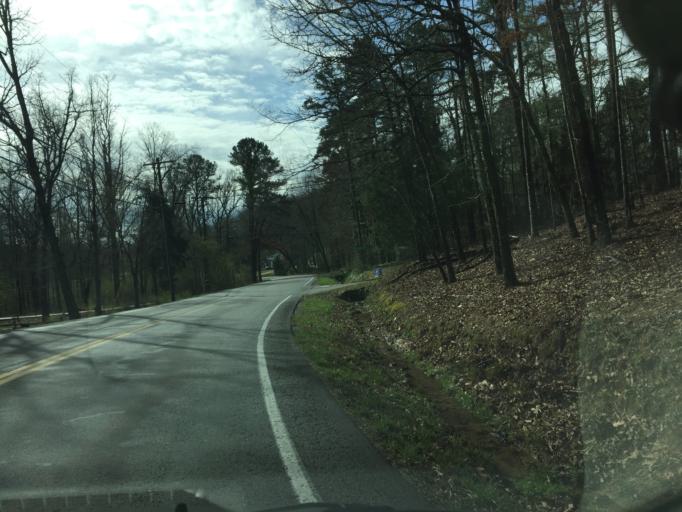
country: US
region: Tennessee
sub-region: Hamilton County
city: Collegedale
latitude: 35.0266
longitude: -85.1007
